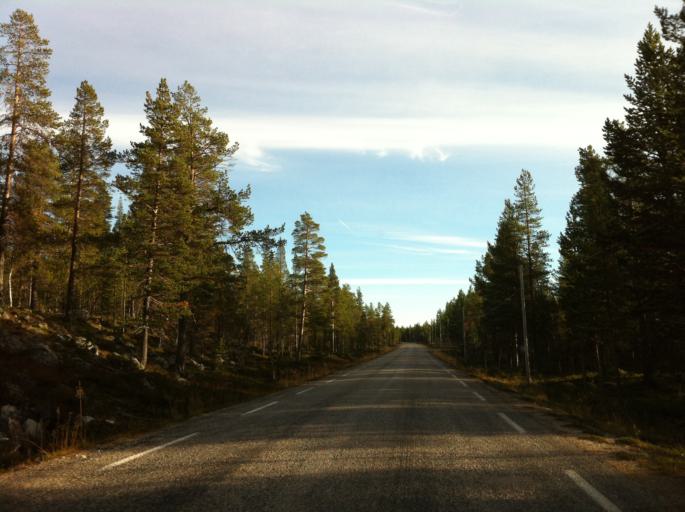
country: NO
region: Hedmark
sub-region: Engerdal
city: Engerdal
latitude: 62.1471
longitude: 11.9574
